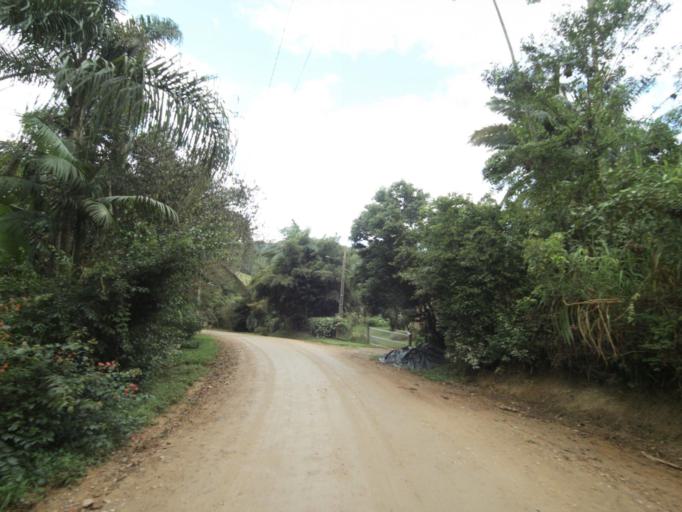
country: BR
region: Santa Catarina
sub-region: Pomerode
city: Pomerode
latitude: -26.7027
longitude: -49.2210
